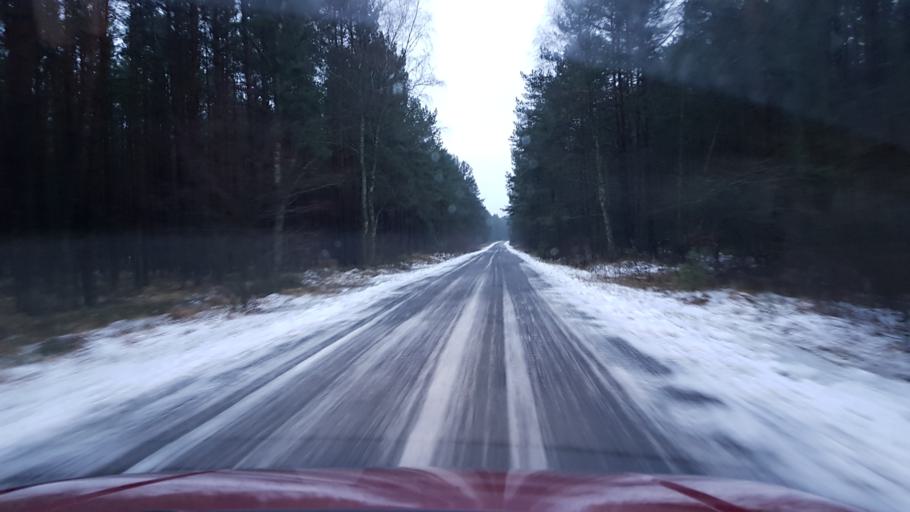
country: PL
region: West Pomeranian Voivodeship
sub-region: Powiat goleniowski
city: Goleniow
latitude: 53.4726
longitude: 14.8320
